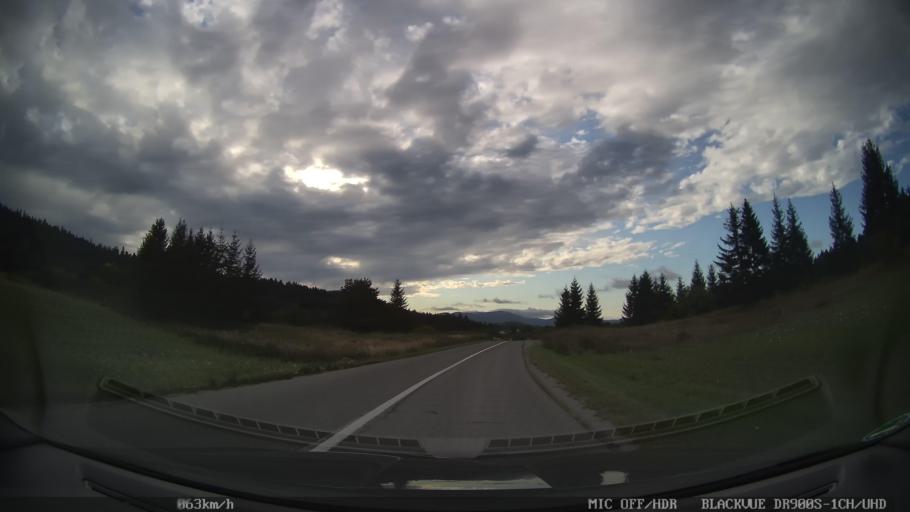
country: HR
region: Licko-Senjska
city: Jezerce
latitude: 44.9690
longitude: 15.5116
